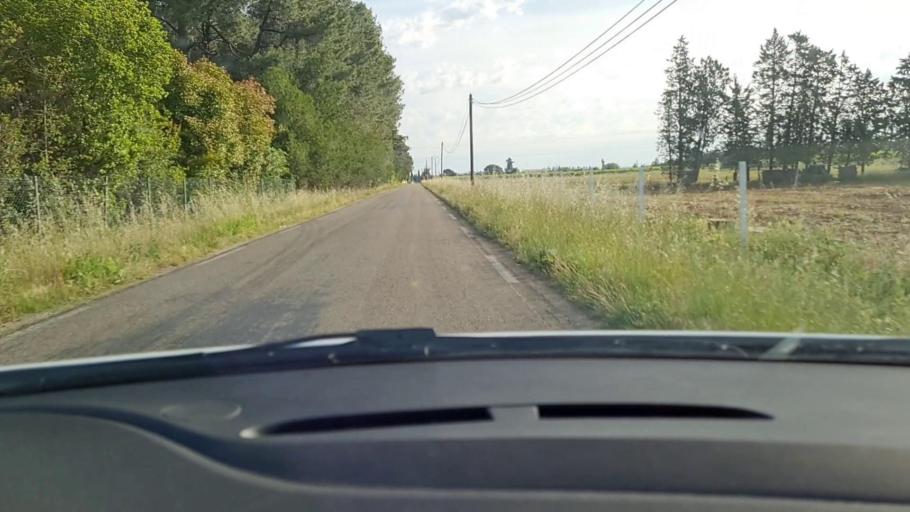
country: FR
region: Languedoc-Roussillon
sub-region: Departement du Gard
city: Bellegarde
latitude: 43.7914
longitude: 4.5299
